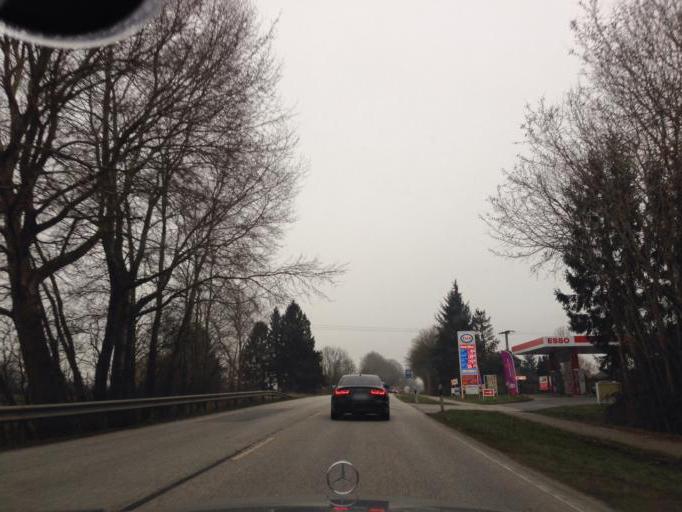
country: DE
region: Schleswig-Holstein
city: Kirchbarkau
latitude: 54.2133
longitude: 10.1487
